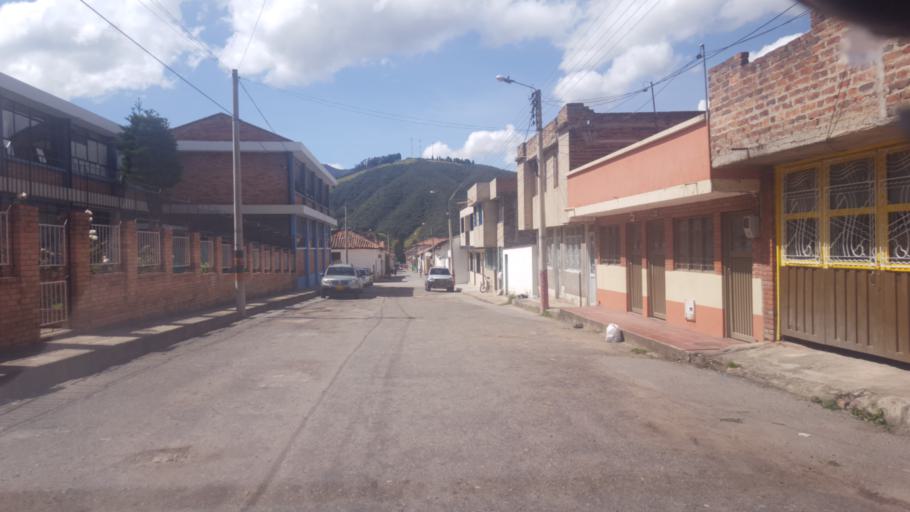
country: CO
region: Boyaca
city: Belen
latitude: 5.9918
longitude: -72.9149
